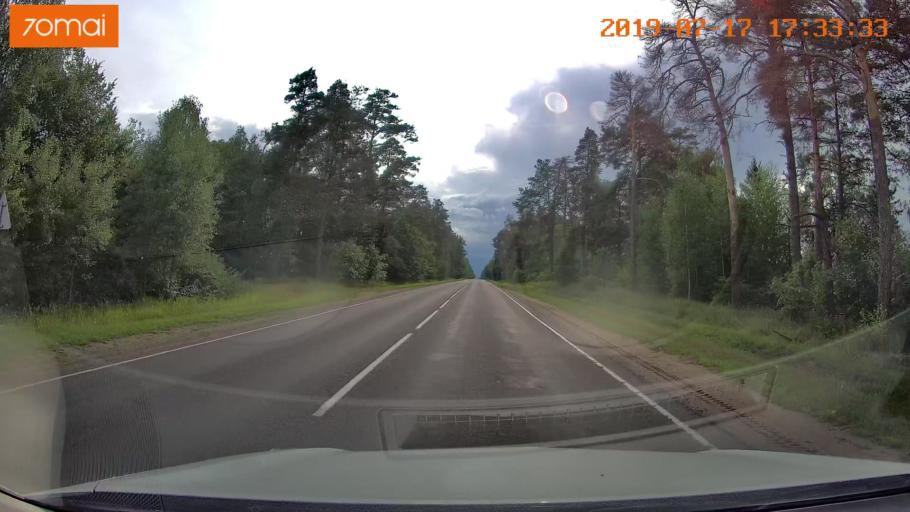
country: BY
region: Mogilev
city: Babruysk
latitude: 53.1110
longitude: 29.0894
